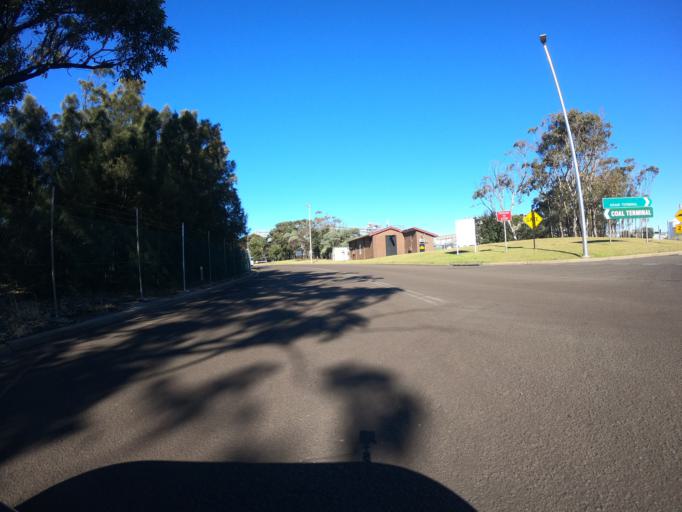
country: AU
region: New South Wales
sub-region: Wollongong
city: Coniston
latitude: -34.4478
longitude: 150.8974
